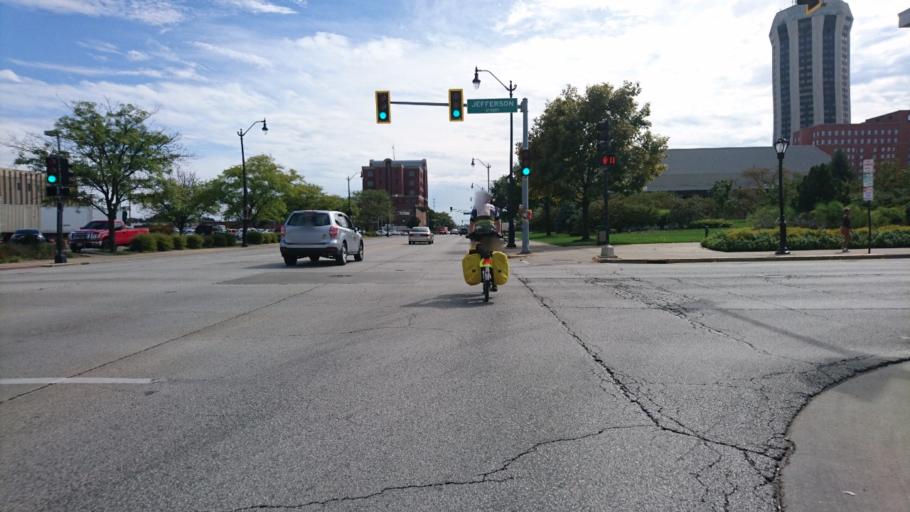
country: US
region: Illinois
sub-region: Sangamon County
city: Springfield
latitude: 39.8030
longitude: -89.6437
